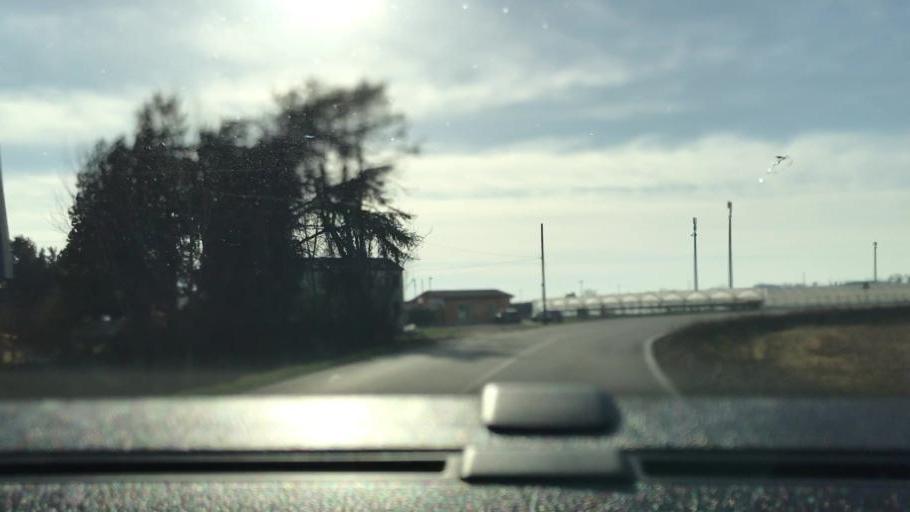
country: IT
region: Veneto
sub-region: Provincia di Rovigo
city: Baruchella
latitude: 45.0700
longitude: 11.4585
